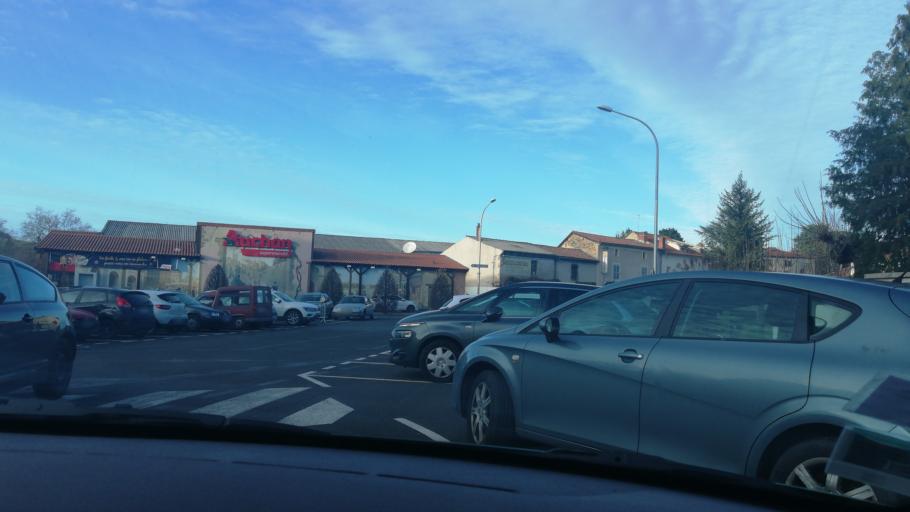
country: FR
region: Auvergne
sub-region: Departement du Puy-de-Dome
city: Billom
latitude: 45.7241
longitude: 3.3395
